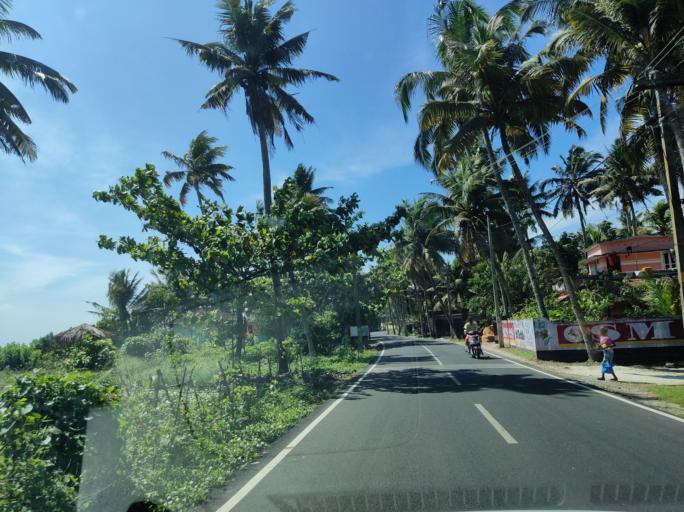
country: IN
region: Kerala
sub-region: Alappuzha
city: Kayankulam
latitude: 9.2051
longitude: 76.4324
